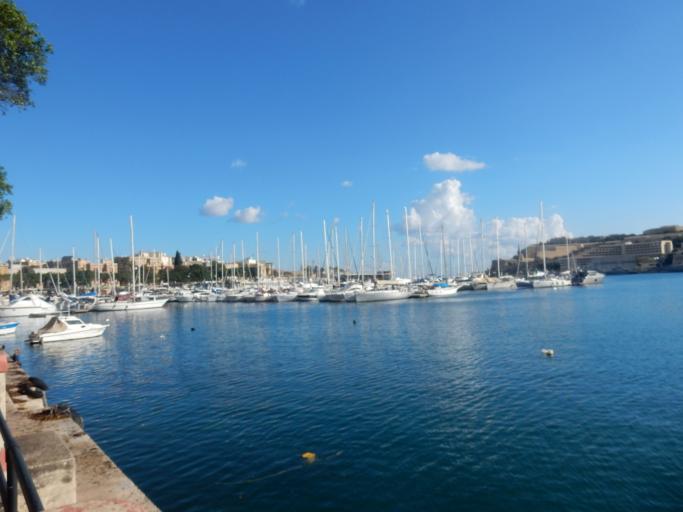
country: MT
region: Tal-Pieta
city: Pieta
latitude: 35.8961
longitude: 14.4975
